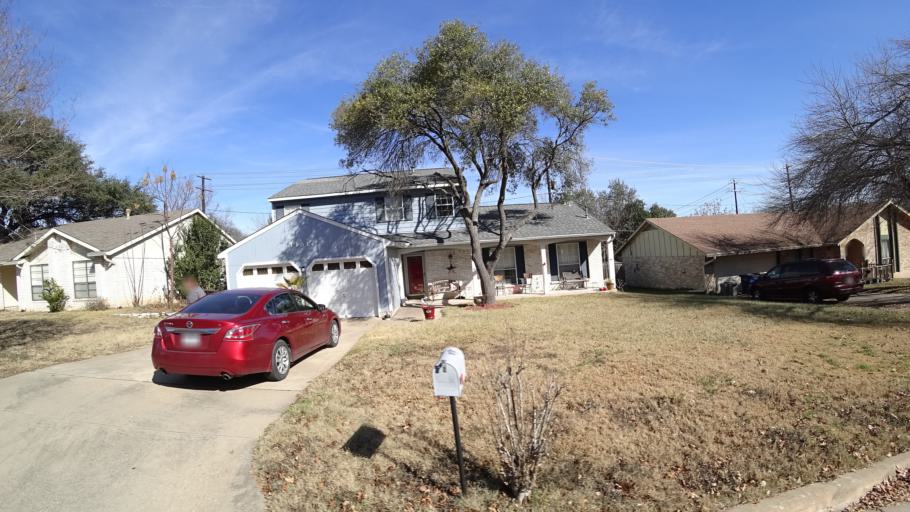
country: US
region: Texas
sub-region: Travis County
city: Wells Branch
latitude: 30.3898
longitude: -97.6861
